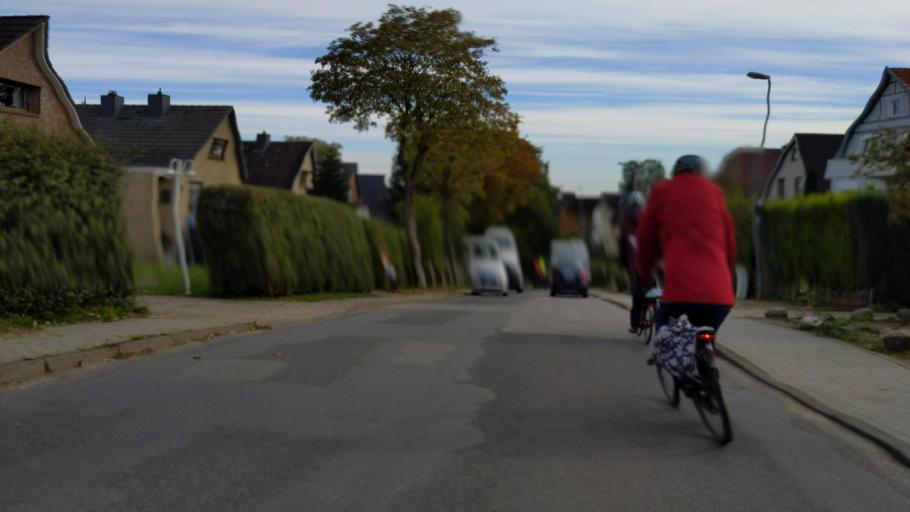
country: DE
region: Schleswig-Holstein
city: Reinfeld
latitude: 53.8332
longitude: 10.4678
